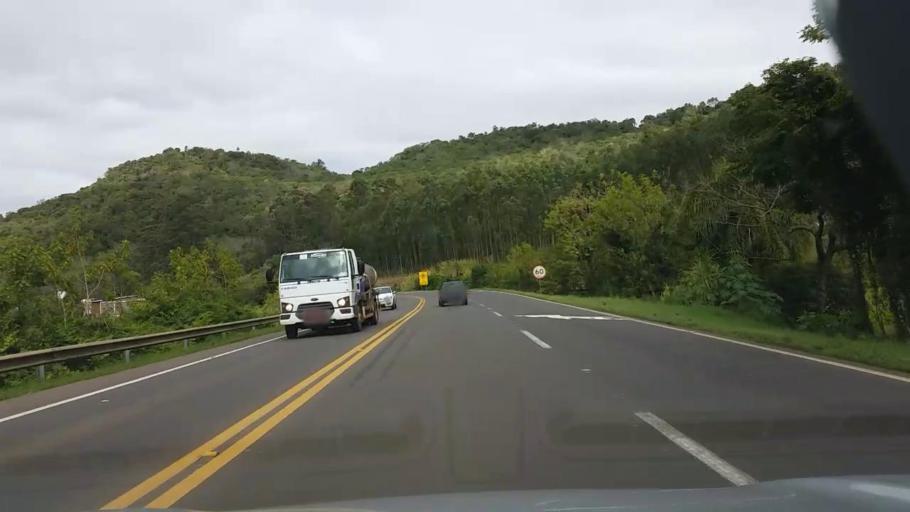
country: BR
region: Rio Grande do Sul
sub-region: Arroio Do Meio
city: Arroio do Meio
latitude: -29.3825
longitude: -52.0544
